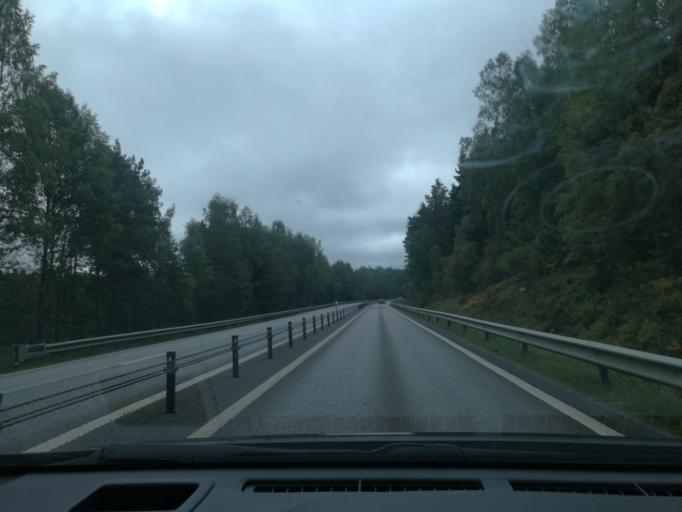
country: SE
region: OEstergoetland
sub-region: Norrkopings Kommun
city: Jursla
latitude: 58.7540
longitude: 16.1757
